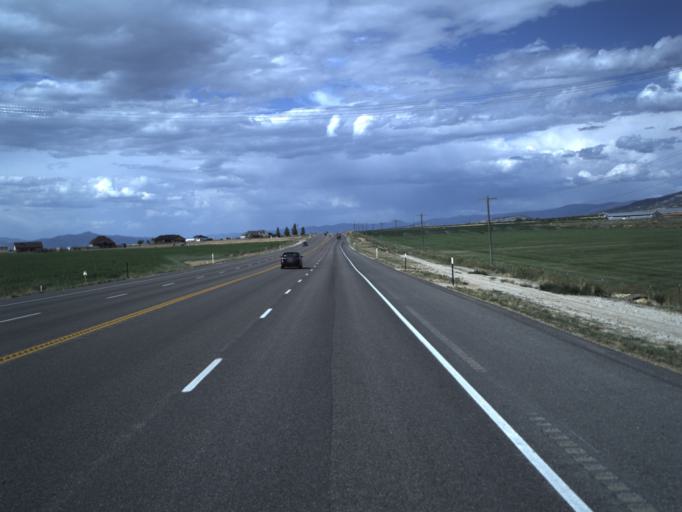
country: US
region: Utah
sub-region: Sanpete County
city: Manti
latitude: 39.2997
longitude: -111.6187
